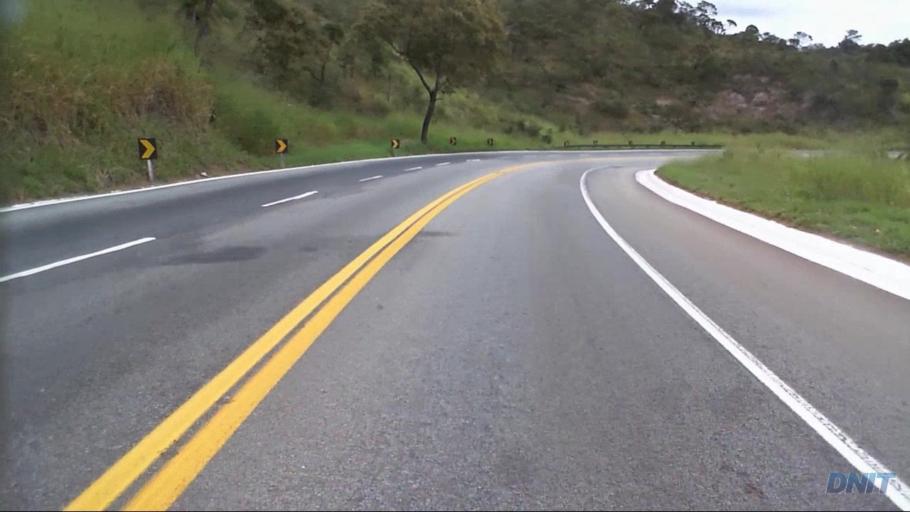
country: BR
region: Minas Gerais
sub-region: Caete
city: Caete
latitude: -19.7885
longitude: -43.7039
